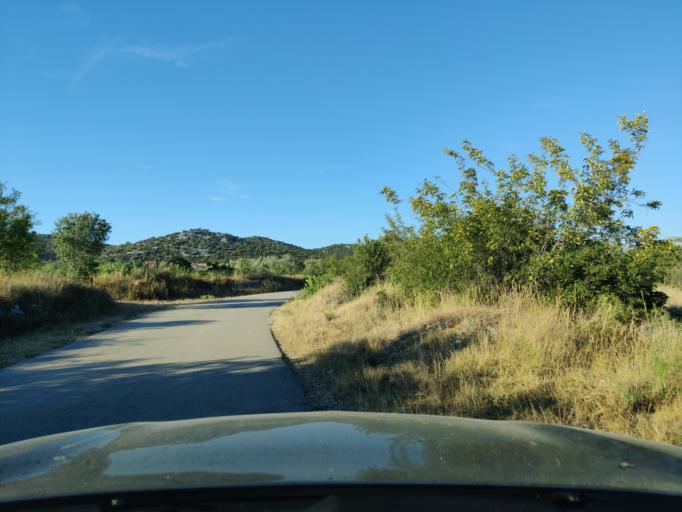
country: HR
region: Sibensko-Kniniska
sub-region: Grad Sibenik
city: Pirovac
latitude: 43.8612
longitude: 15.7041
